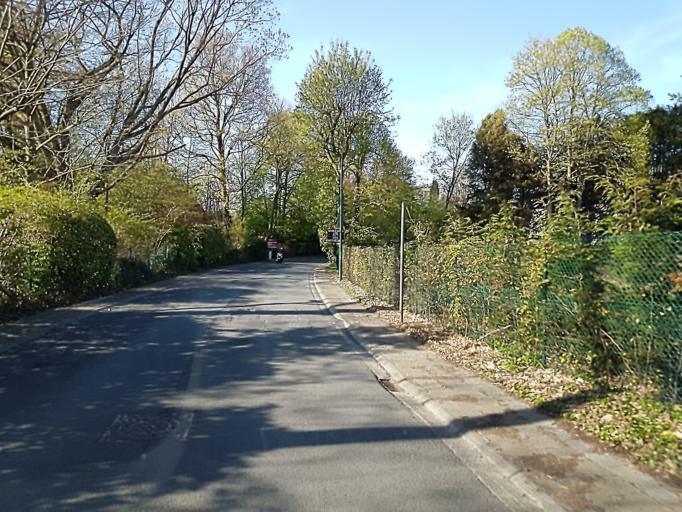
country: BE
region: Flanders
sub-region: Provincie Vlaams-Brabant
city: Sint-Genesius-Rode
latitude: 50.7630
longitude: 4.3748
